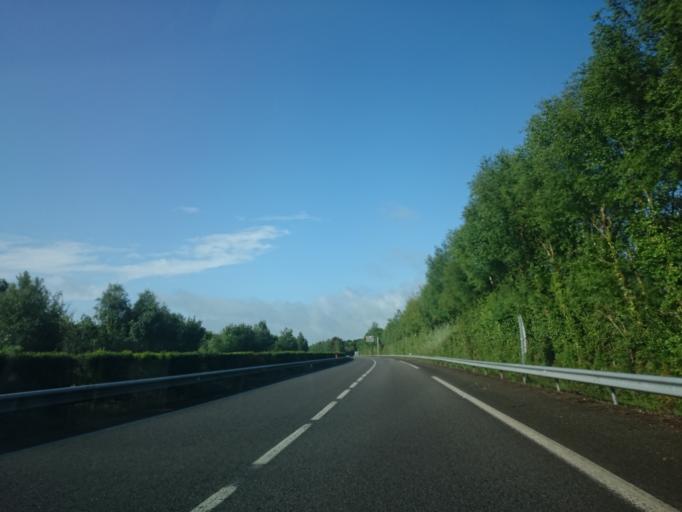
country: FR
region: Brittany
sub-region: Departement du Morbihan
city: Elven
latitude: 47.7433
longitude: -2.5745
